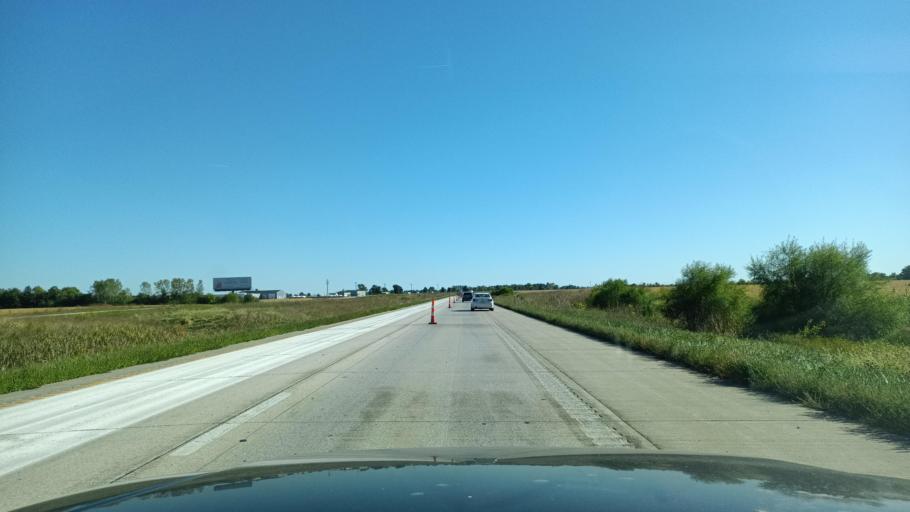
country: US
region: Missouri
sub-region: Randolph County
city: Moberly
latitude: 39.4931
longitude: -92.4353
